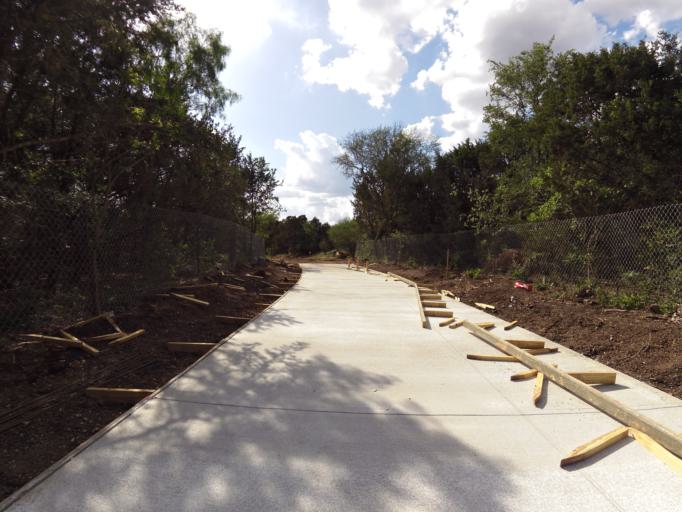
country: US
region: Texas
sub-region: Bexar County
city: Shavano Park
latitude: 29.5990
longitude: -98.5973
